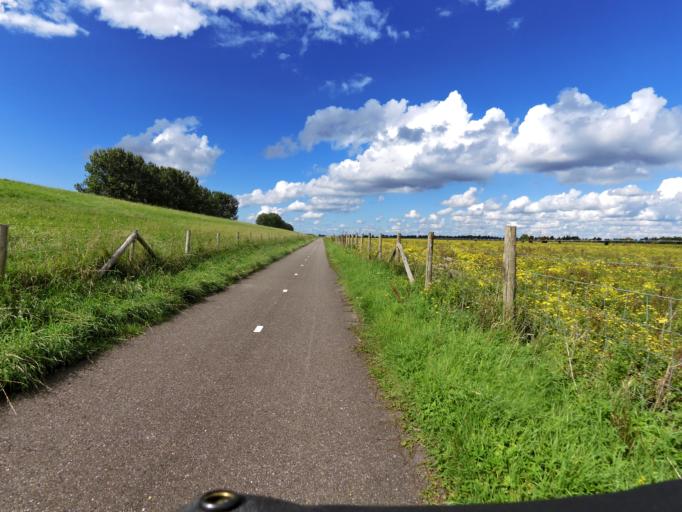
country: NL
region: North Brabant
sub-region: Gemeente Steenbergen
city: Dinteloord
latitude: 51.6883
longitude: 4.3575
